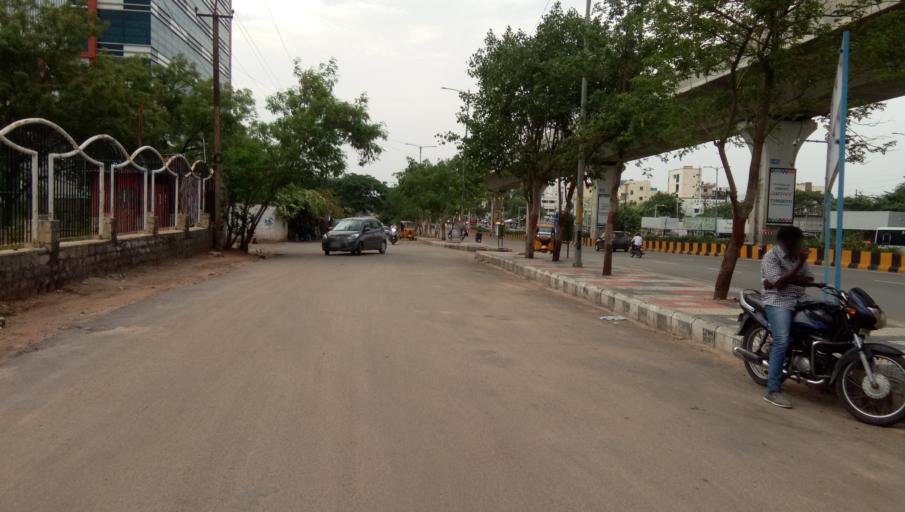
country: IN
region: Telangana
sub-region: Rangareddi
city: Lal Bahadur Nagar
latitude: 17.3540
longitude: 78.5457
